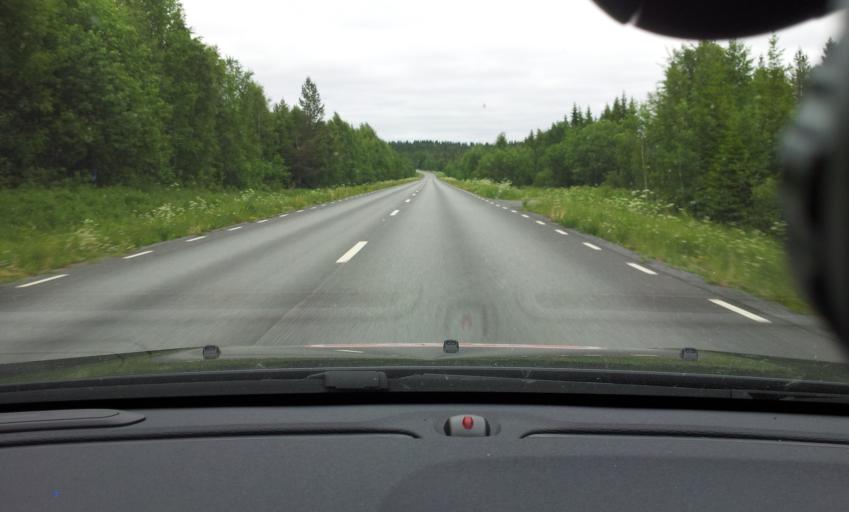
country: SE
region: Jaemtland
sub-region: Krokoms Kommun
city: Krokom
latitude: 63.0880
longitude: 14.2977
